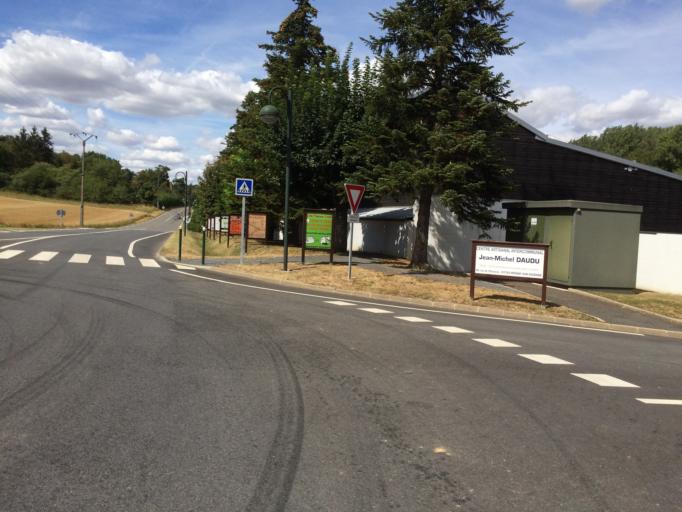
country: FR
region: Ile-de-France
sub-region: Departement de l'Essonne
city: Maisse
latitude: 48.3527
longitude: 2.3805
